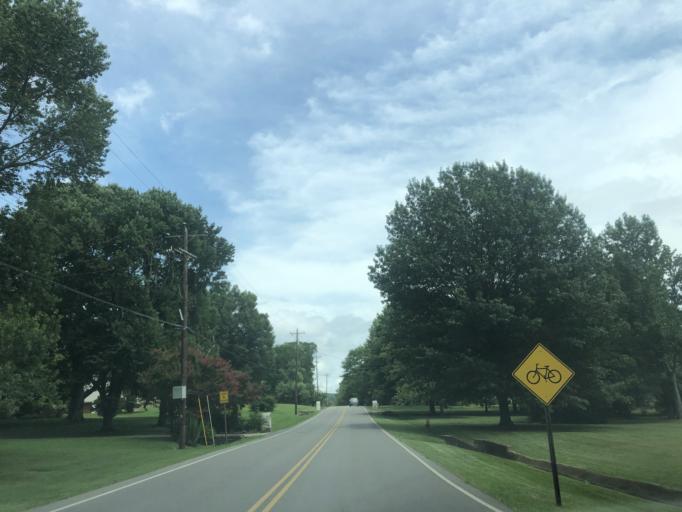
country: US
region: Tennessee
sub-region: Davidson County
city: Forest Hills
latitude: 36.0647
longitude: -86.8206
